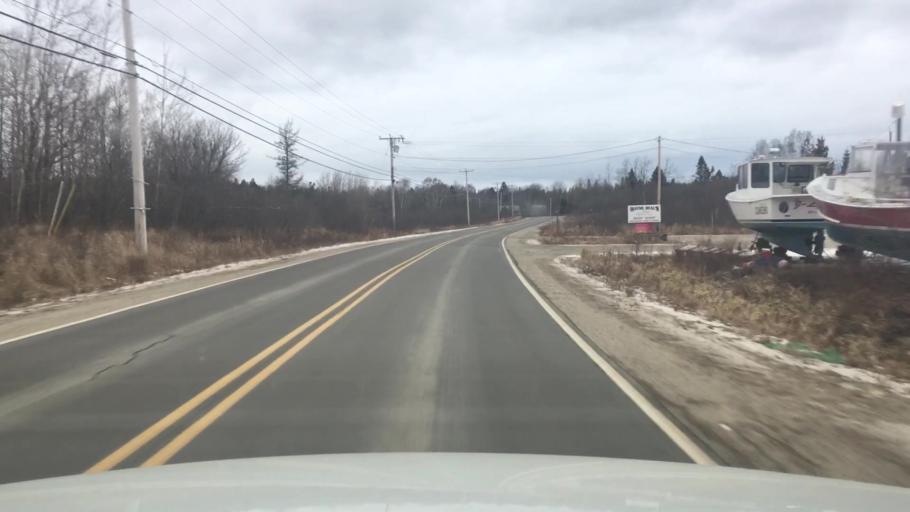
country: US
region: Maine
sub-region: Washington County
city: Jonesport
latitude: 44.5541
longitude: -67.6253
